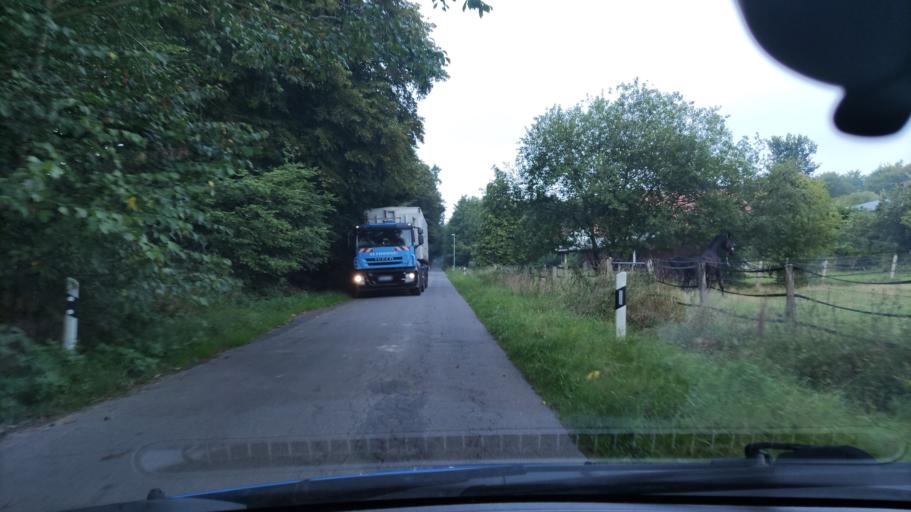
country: DE
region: Lower Saxony
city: Altenmedingen
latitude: 53.1413
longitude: 10.5904
